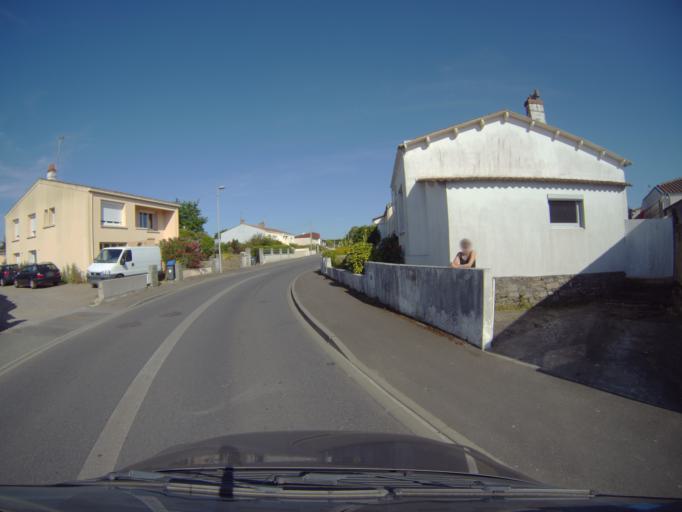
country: FR
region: Pays de la Loire
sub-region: Departement de la Vendee
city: Les Sables-d'Olonne
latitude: 46.5011
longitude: -1.7719
